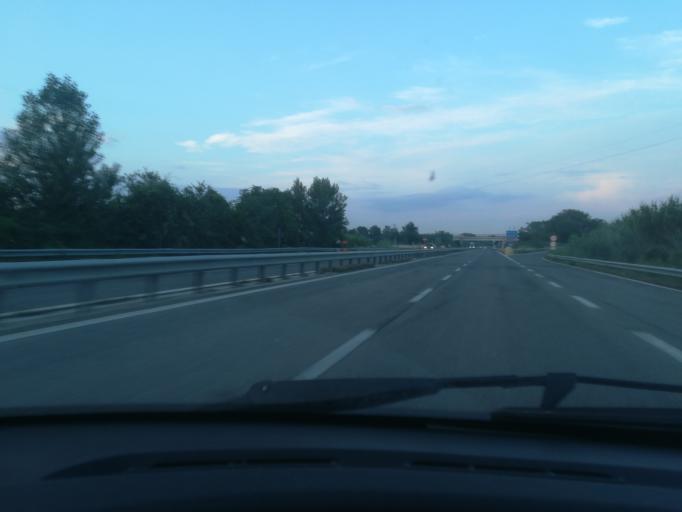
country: IT
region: The Marches
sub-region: Provincia di Macerata
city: Casette Verdini
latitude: 43.2404
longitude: 13.4111
